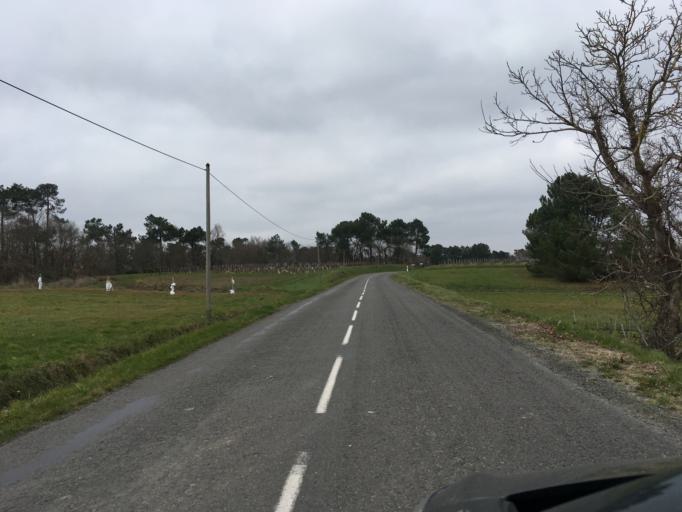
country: FR
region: Aquitaine
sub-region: Departement de la Gironde
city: Saint-Ciers-sur-Gironde
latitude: 45.3268
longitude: -0.5943
